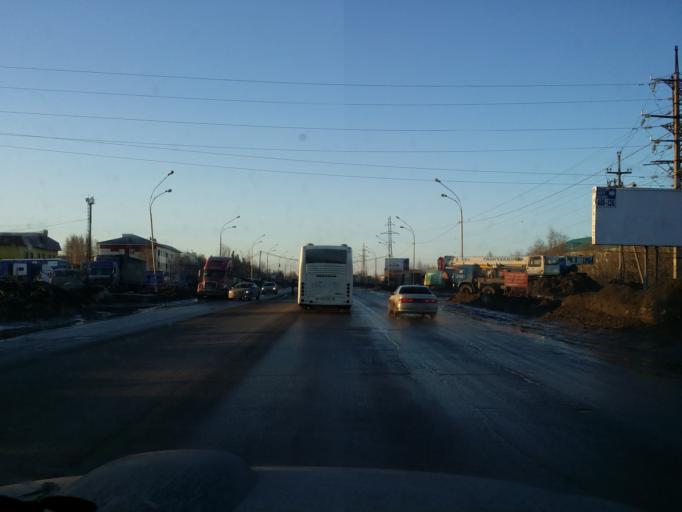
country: RU
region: Khanty-Mansiyskiy Avtonomnyy Okrug
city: Nizhnevartovsk
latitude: 60.9524
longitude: 76.5299
